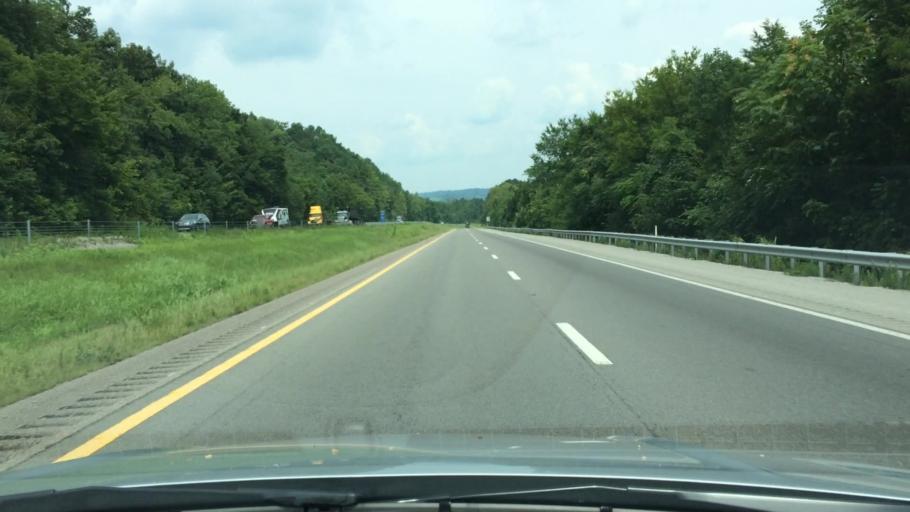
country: US
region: Tennessee
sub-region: Marshall County
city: Cornersville
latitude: 35.2629
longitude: -86.8852
